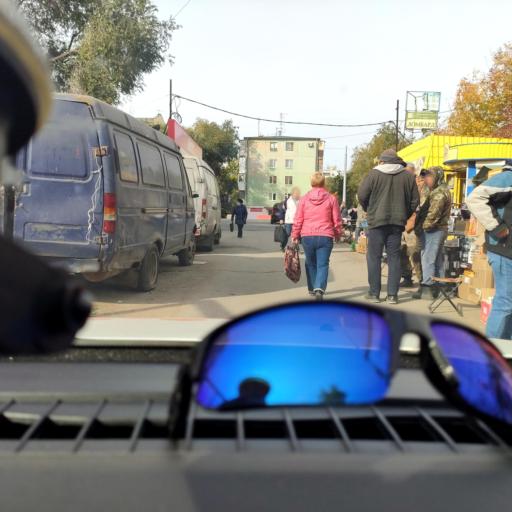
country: RU
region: Samara
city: Samara
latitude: 53.1218
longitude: 50.0885
